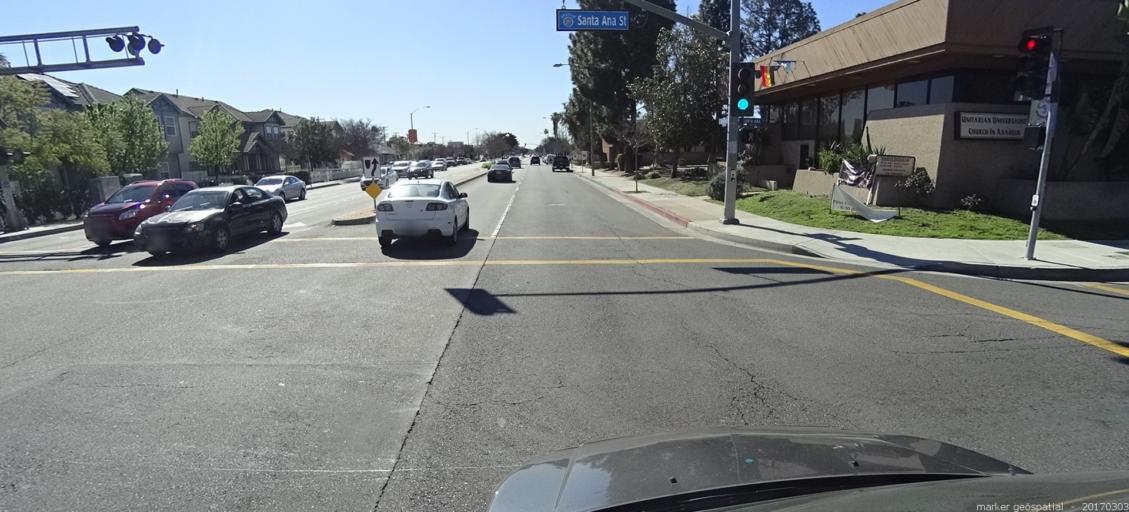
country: US
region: California
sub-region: Orange County
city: Anaheim
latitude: 33.8299
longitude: -117.9182
